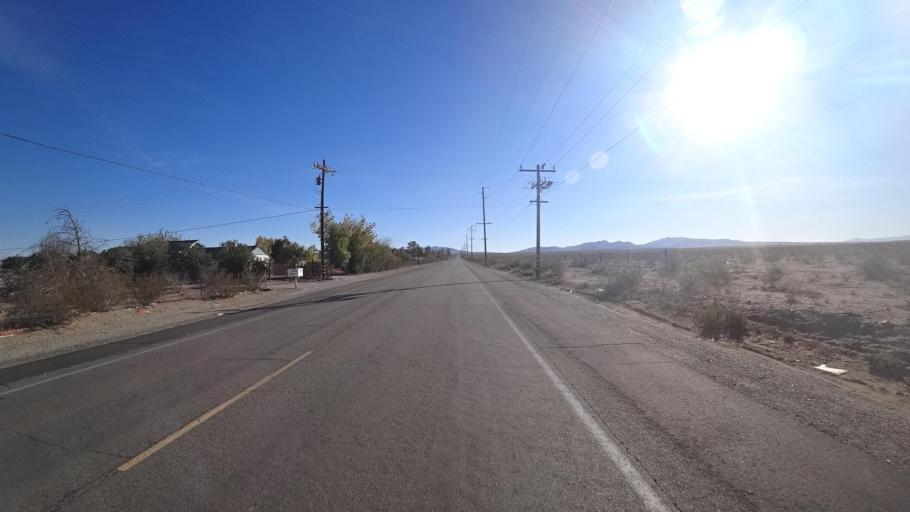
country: US
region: California
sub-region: Kern County
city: China Lake Acres
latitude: 35.6338
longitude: -117.7231
